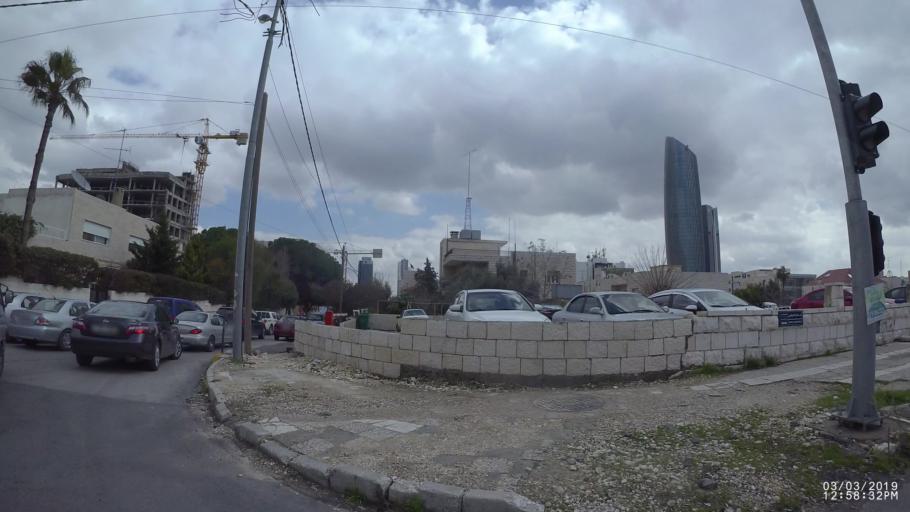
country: JO
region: Amman
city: Amman
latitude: 31.9689
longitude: 35.9023
